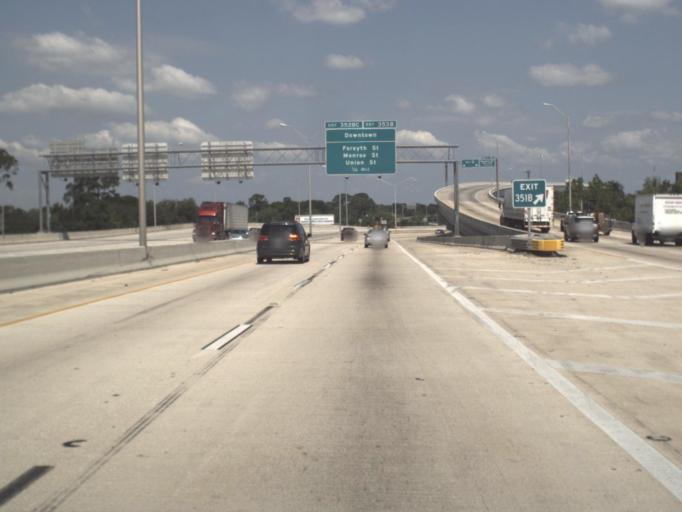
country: US
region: Florida
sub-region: Duval County
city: Jacksonville
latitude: 30.3176
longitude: -81.6781
